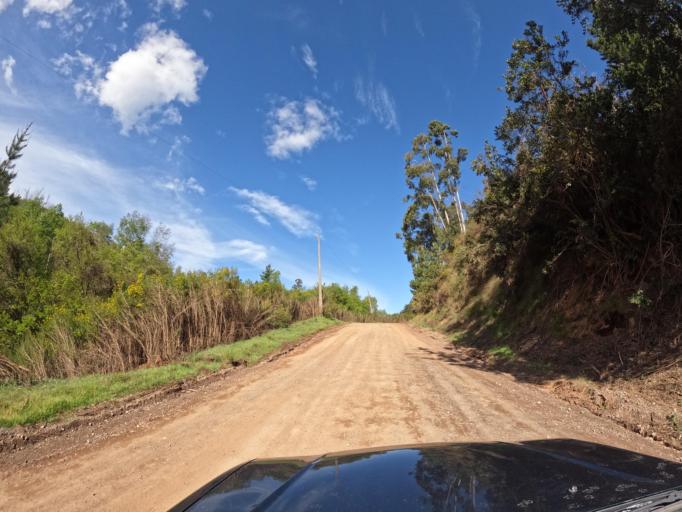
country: CL
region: Biobio
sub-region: Provincia de Concepcion
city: Chiguayante
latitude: -37.0716
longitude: -72.8434
